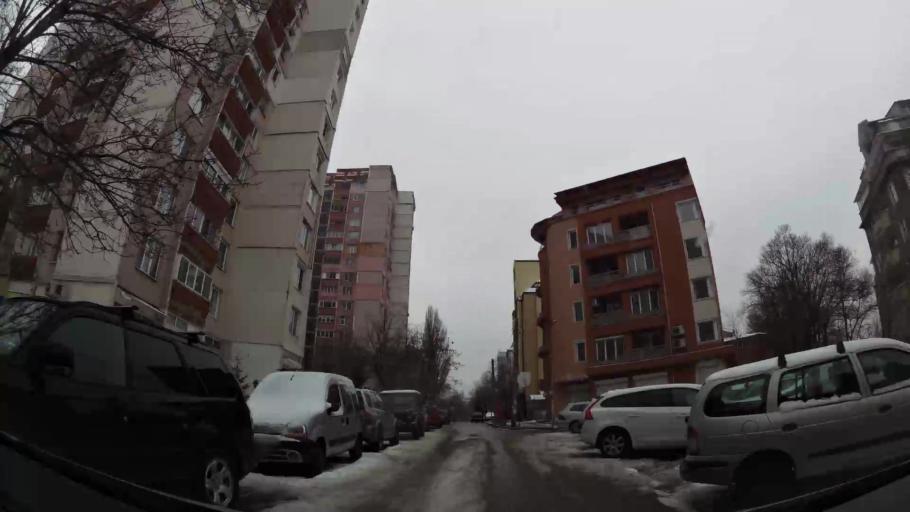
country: BG
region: Sofia-Capital
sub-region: Stolichna Obshtina
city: Sofia
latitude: 42.7112
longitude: 23.3123
